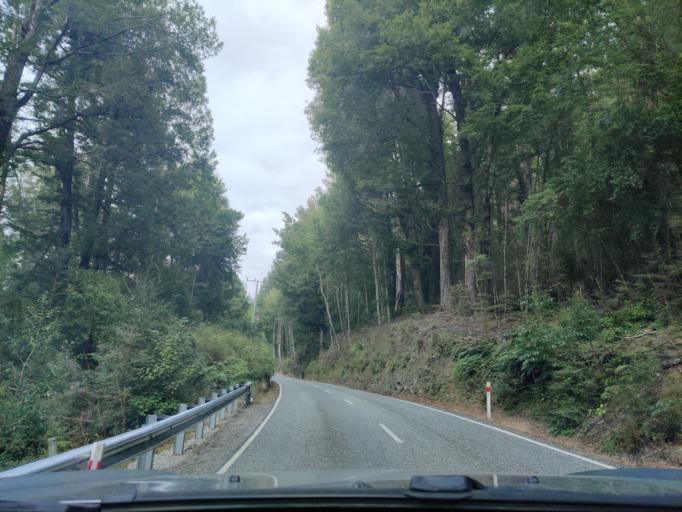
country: NZ
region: Otago
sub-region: Queenstown-Lakes District
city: Queenstown
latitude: -45.0711
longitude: 168.4991
